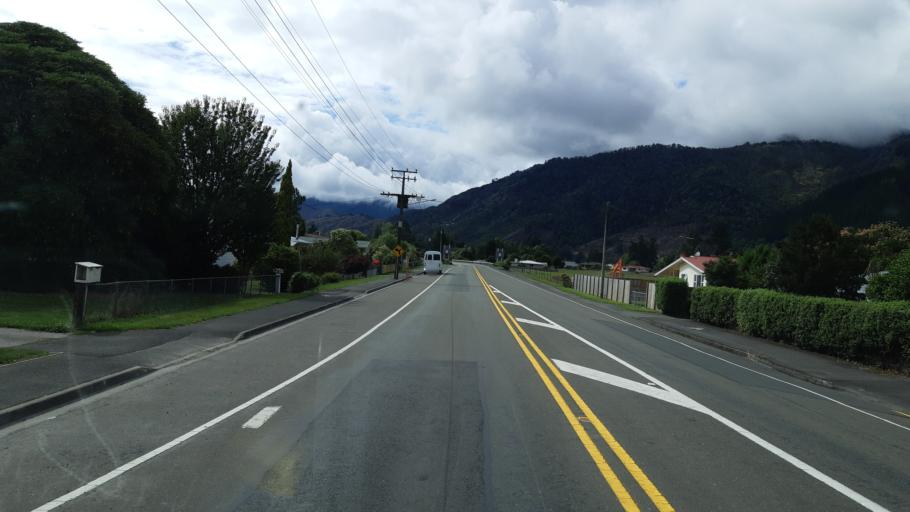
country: NZ
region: West Coast
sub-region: Buller District
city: Westport
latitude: -41.8001
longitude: 172.3325
